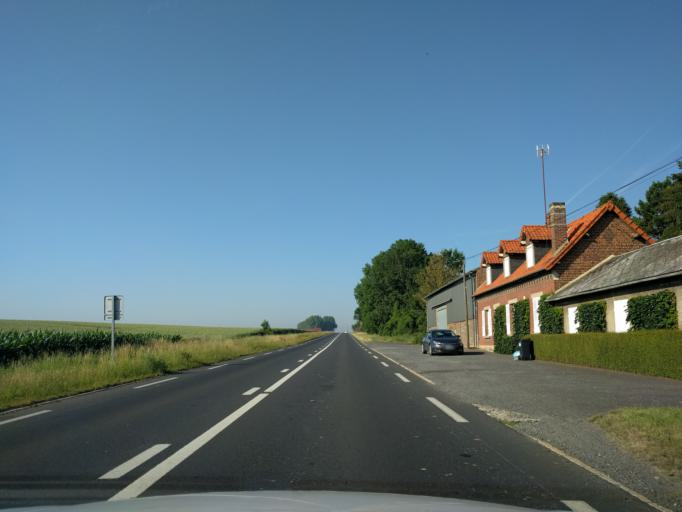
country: FR
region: Picardie
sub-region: Departement de la Somme
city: Chaulnes
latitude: 49.7768
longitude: 2.8224
